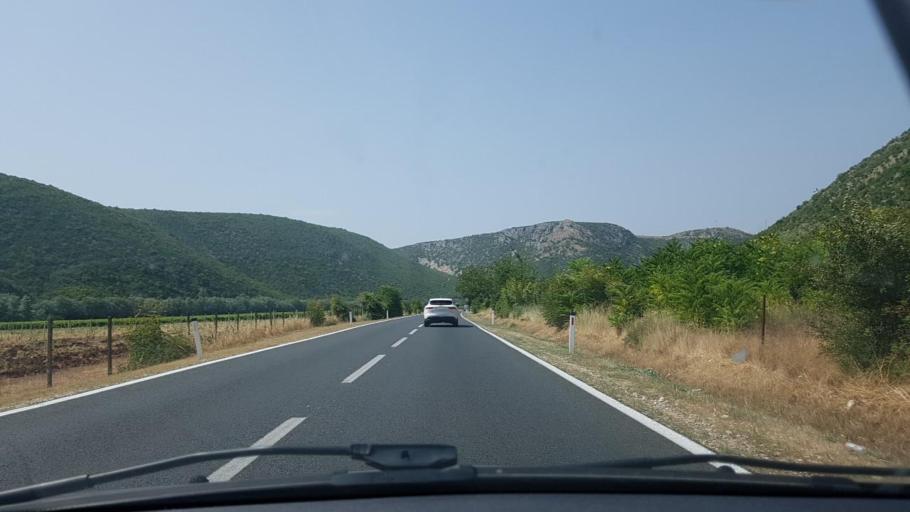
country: BA
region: Federation of Bosnia and Herzegovina
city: Citluk
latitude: 43.1837
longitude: 17.7834
